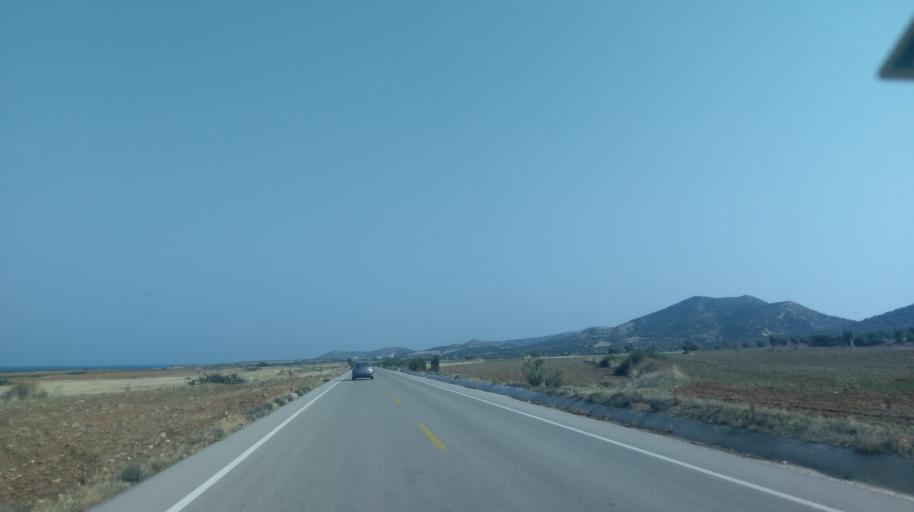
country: CY
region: Ammochostos
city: Leonarisso
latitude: 35.4752
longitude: 34.0511
